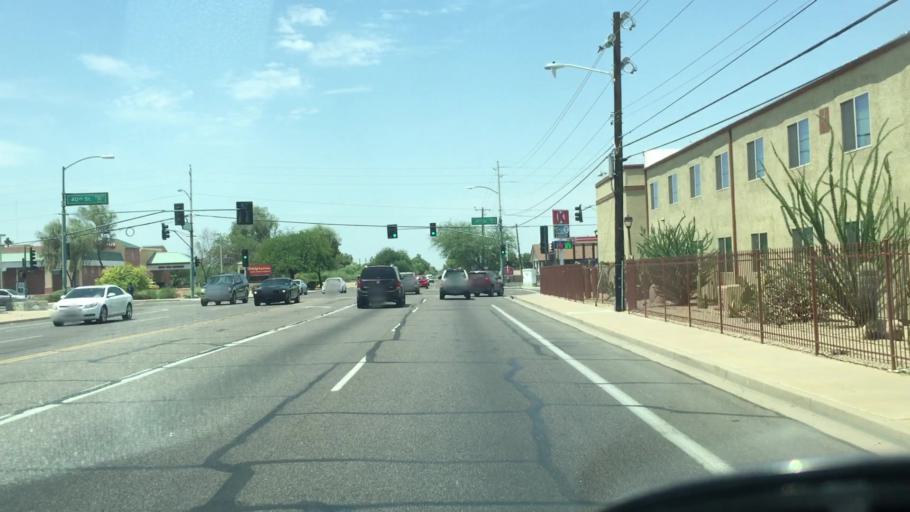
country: US
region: Arizona
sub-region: Maricopa County
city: Guadalupe
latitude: 33.3927
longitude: -111.9948
